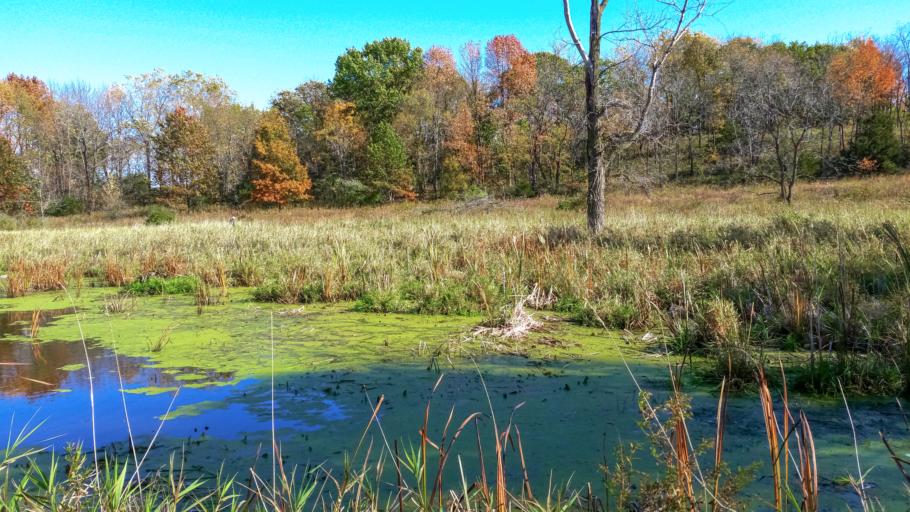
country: US
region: Wisconsin
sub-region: Jefferson County
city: Lake Ripley
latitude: 42.9869
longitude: -88.9810
